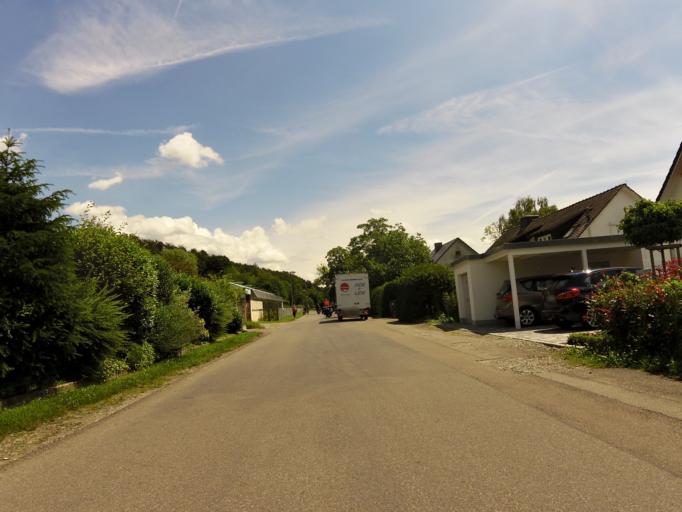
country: DE
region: Baden-Wuerttemberg
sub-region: Tuebingen Region
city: Uberlingen
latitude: 47.7489
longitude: 9.2046
